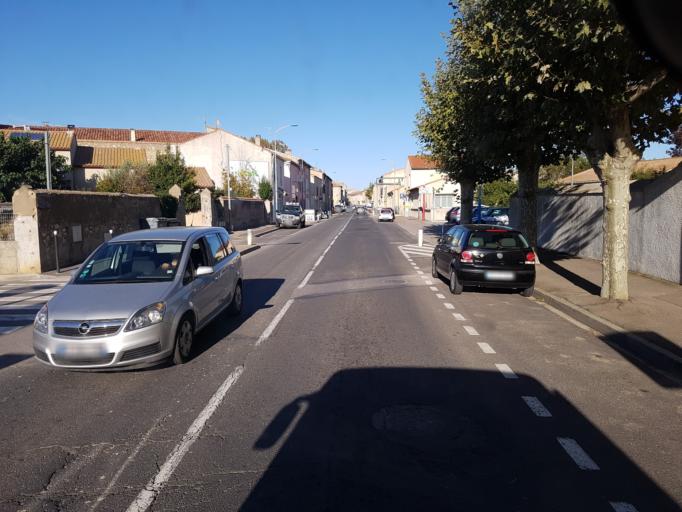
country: FR
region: Languedoc-Roussillon
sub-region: Departement de l'Aude
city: Coursan
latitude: 43.2315
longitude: 3.0541
